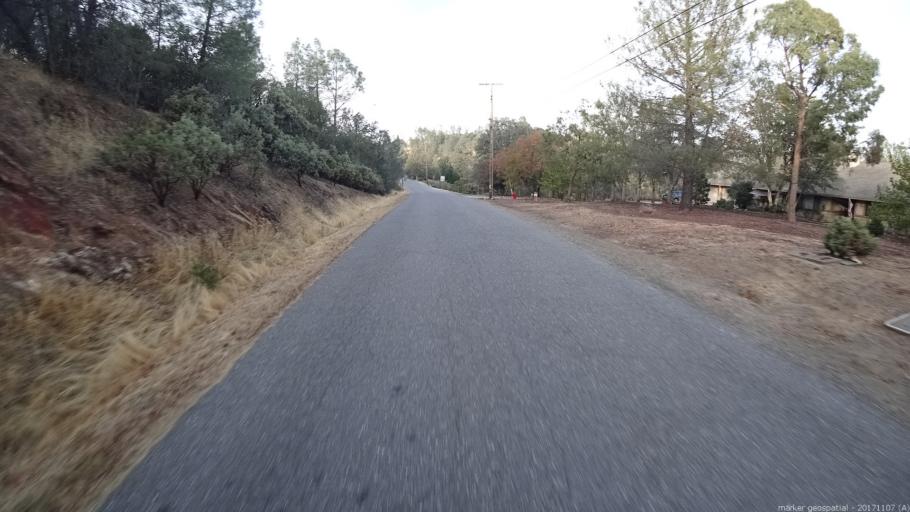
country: US
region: California
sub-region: Shasta County
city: Shasta
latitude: 40.5288
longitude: -122.4860
